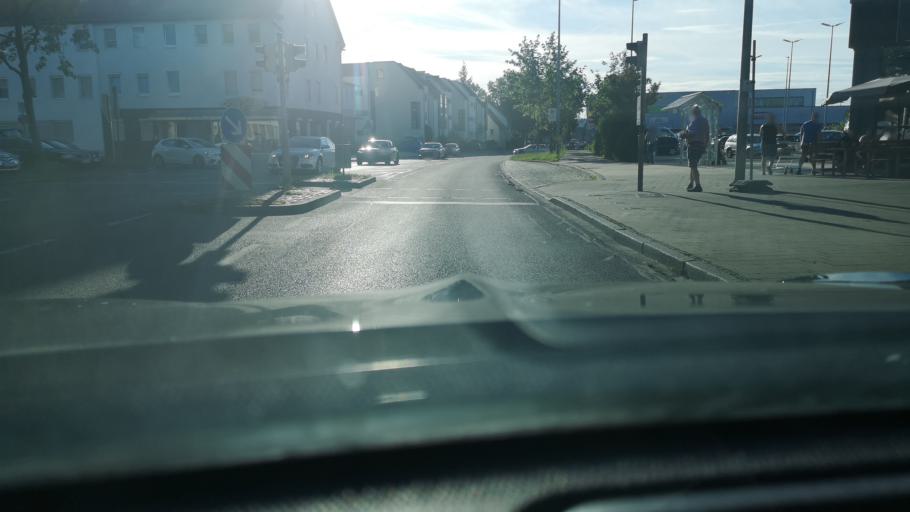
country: DE
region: Baden-Wuerttemberg
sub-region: Tuebingen Region
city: Metzingen
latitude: 48.5402
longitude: 9.2791
